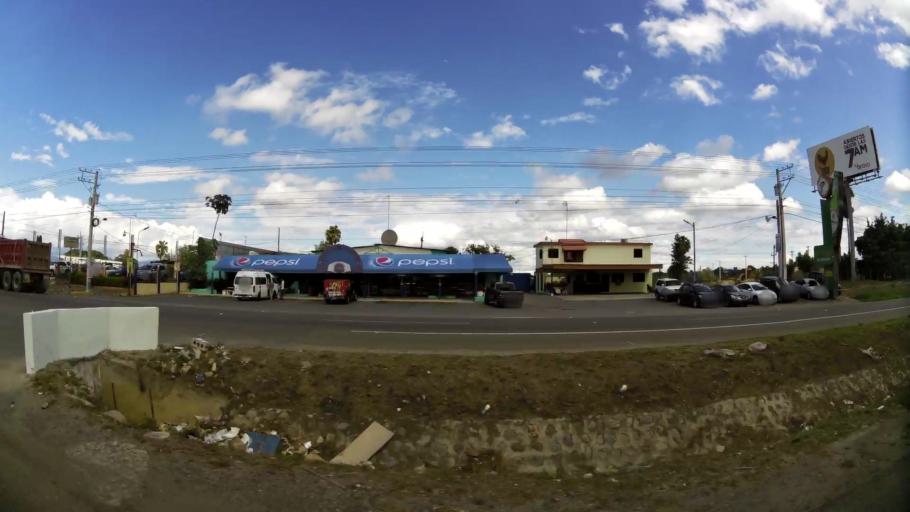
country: DO
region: La Vega
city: Rio Verde Arriba
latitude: 19.3660
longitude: -70.6030
